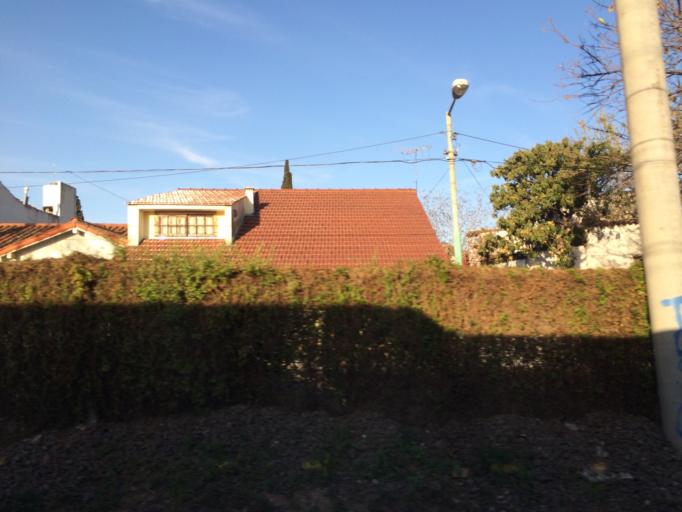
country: AR
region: Buenos Aires
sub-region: Partido de Lomas de Zamora
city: Lomas de Zamora
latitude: -34.7713
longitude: -58.3970
